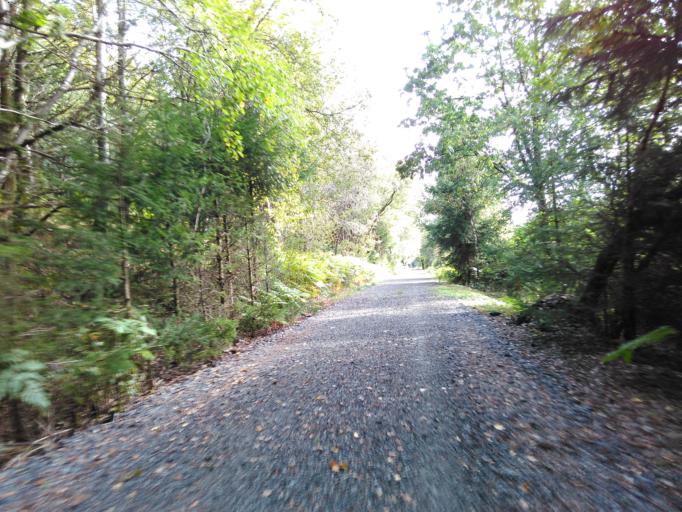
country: BE
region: Wallonia
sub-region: Province du Luxembourg
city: Vaux-sur-Sure
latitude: 49.9400
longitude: 5.5774
